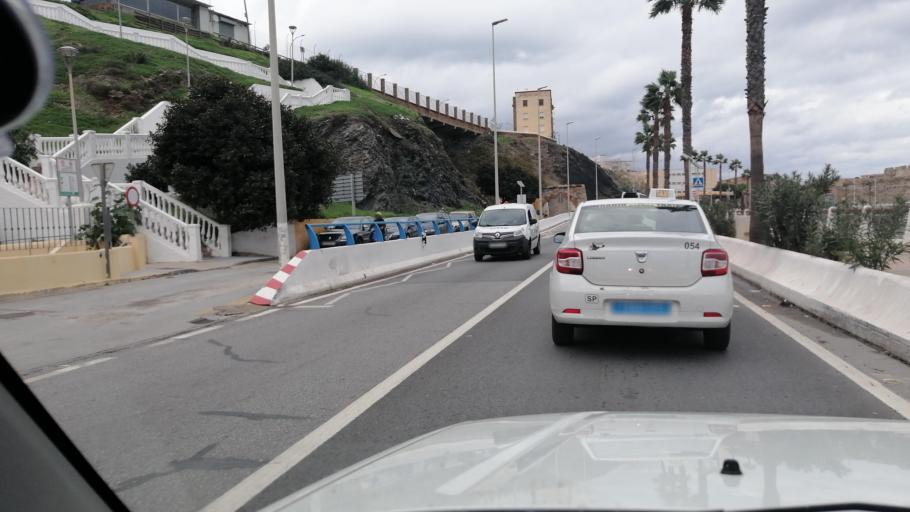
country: ES
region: Ceuta
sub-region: Ceuta
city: Ceuta
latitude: 35.8854
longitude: -5.3224
